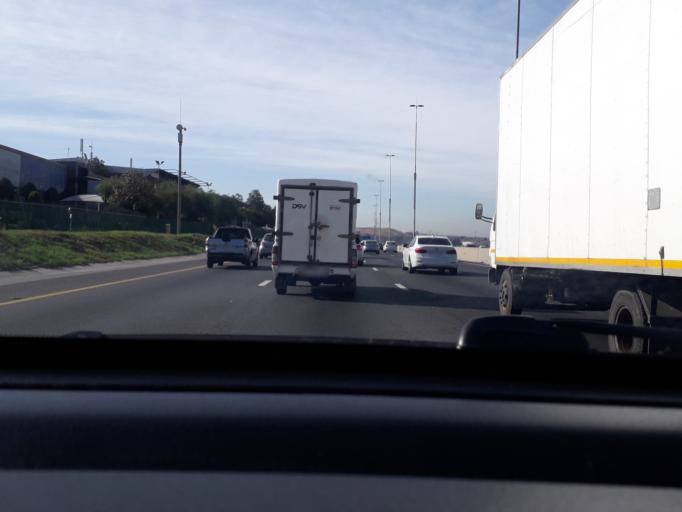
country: ZA
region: Gauteng
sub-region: City of Johannesburg Metropolitan Municipality
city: Modderfontein
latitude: -26.0675
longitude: 28.1103
